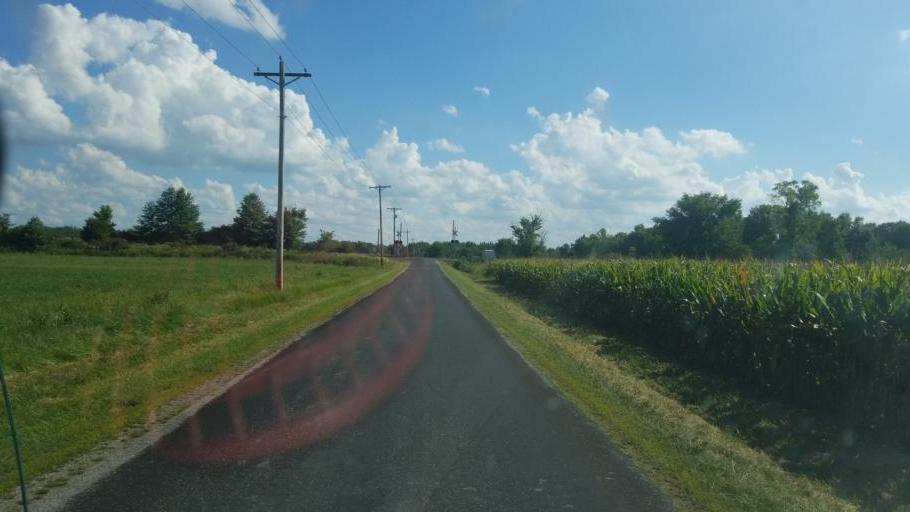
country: US
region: Ohio
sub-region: Union County
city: Richwood
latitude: 40.5858
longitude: -83.3618
